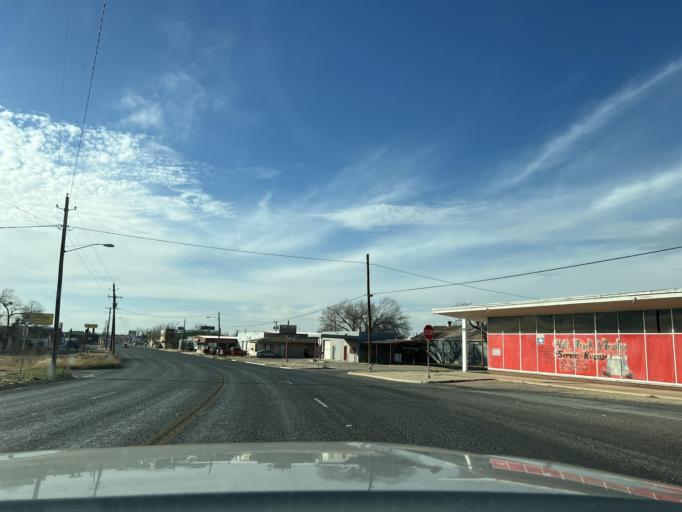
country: US
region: Texas
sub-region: Scurry County
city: Snyder
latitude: 32.7168
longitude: -100.9049
